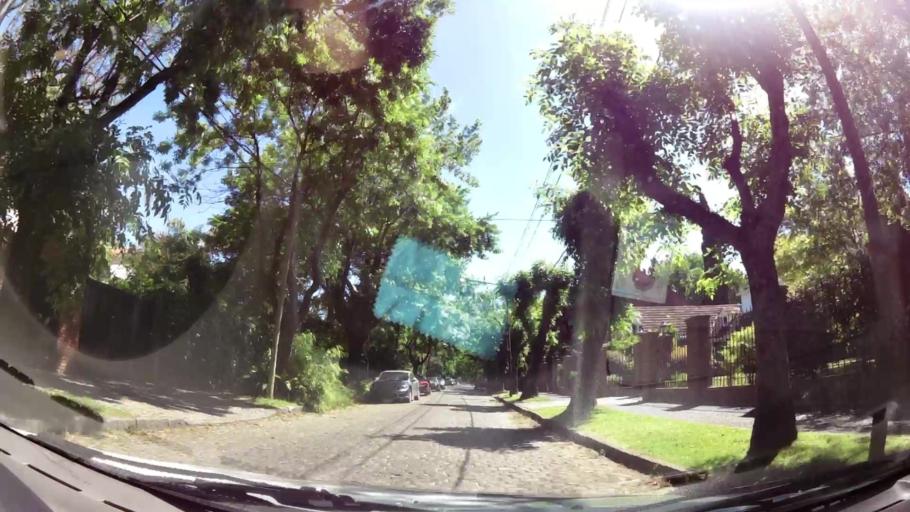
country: AR
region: Buenos Aires
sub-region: Partido de San Isidro
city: San Isidro
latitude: -34.4794
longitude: -58.4903
